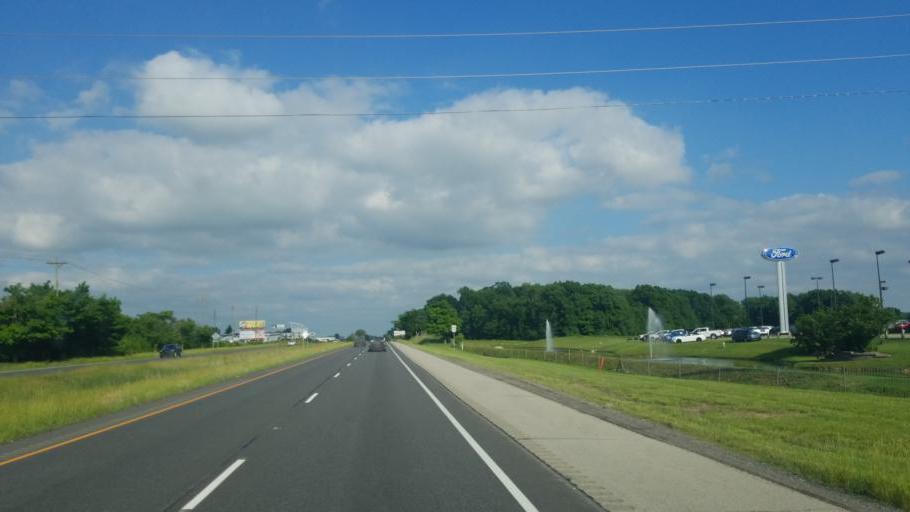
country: US
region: Indiana
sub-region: Whitley County
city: Columbia City
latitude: 41.1403
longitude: -85.4325
